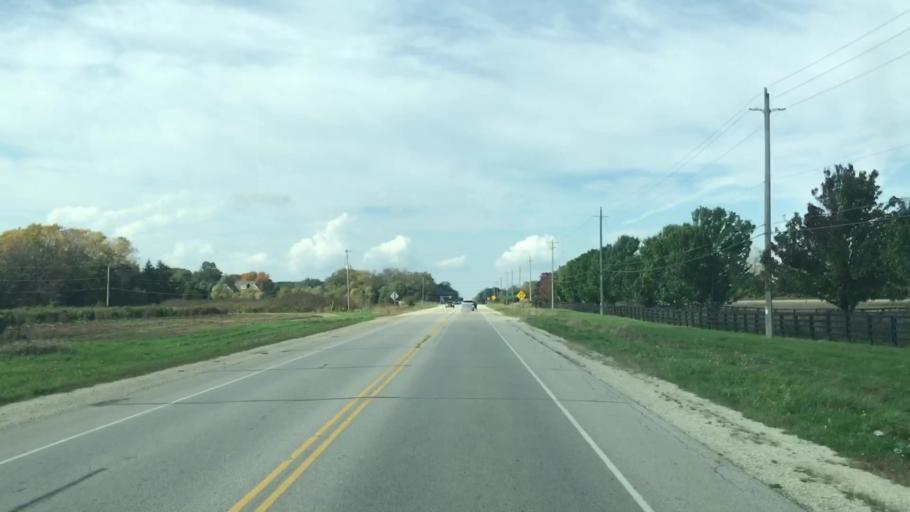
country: US
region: Wisconsin
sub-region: Ozaukee County
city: Mequon
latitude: 43.2215
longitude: -88.0356
